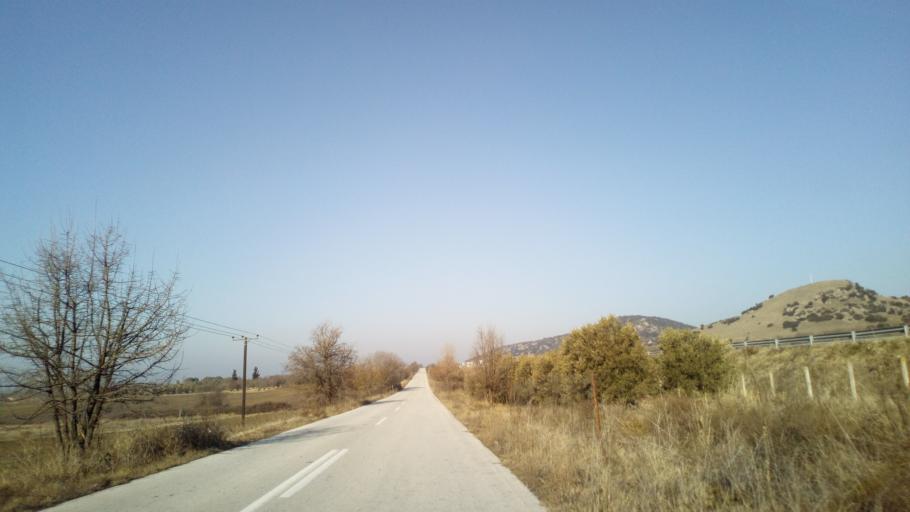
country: GR
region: Central Macedonia
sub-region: Nomos Thessalonikis
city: Gerakarou
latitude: 40.7001
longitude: 23.2037
